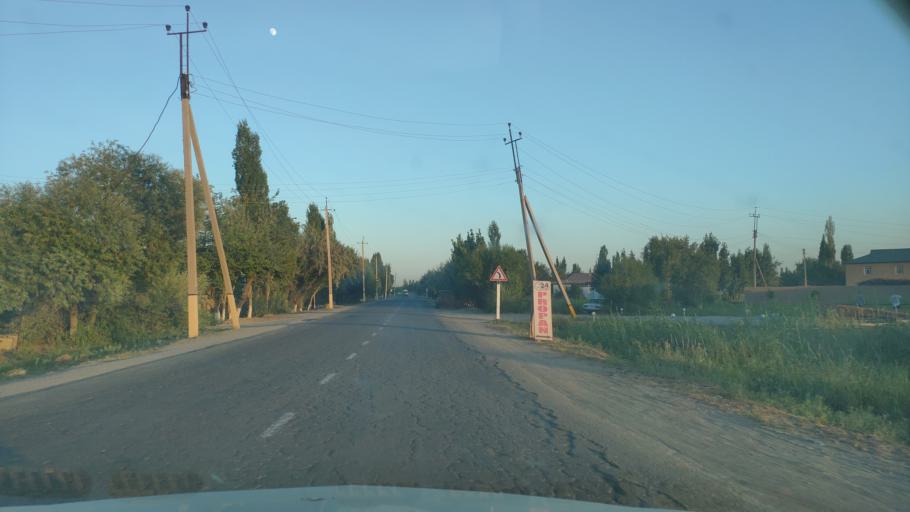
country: UZ
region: Karakalpakstan
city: To'rtko'l Shahri
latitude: 41.5643
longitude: 60.9535
